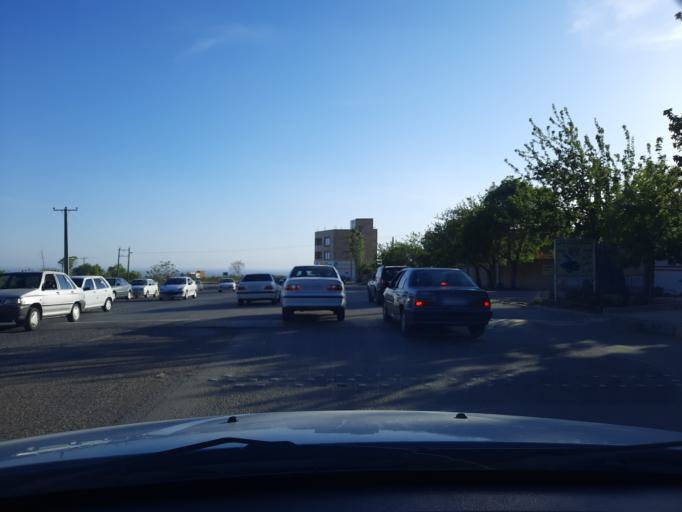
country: IR
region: Qazvin
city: Qazvin
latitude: 36.3300
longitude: 50.1493
